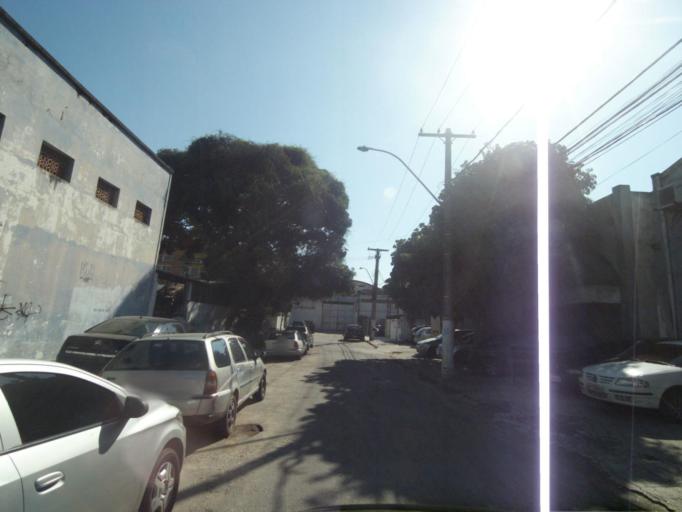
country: BR
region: Rio de Janeiro
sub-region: Niteroi
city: Niteroi
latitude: -22.8871
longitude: -43.1183
